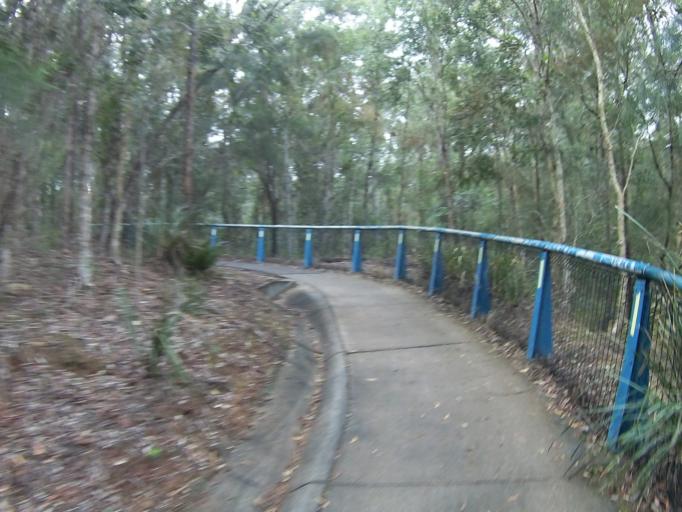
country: AU
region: Queensland
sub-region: Brisbane
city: Nathan
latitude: -27.5437
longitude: 153.0619
